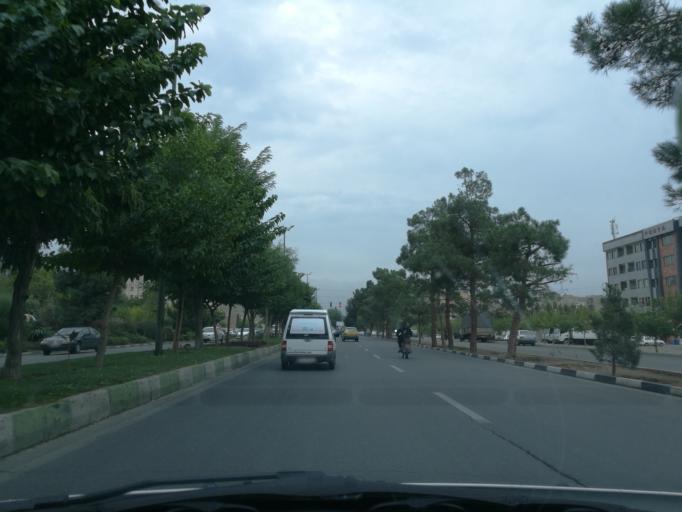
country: IR
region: Alborz
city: Karaj
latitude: 35.8582
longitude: 50.9472
